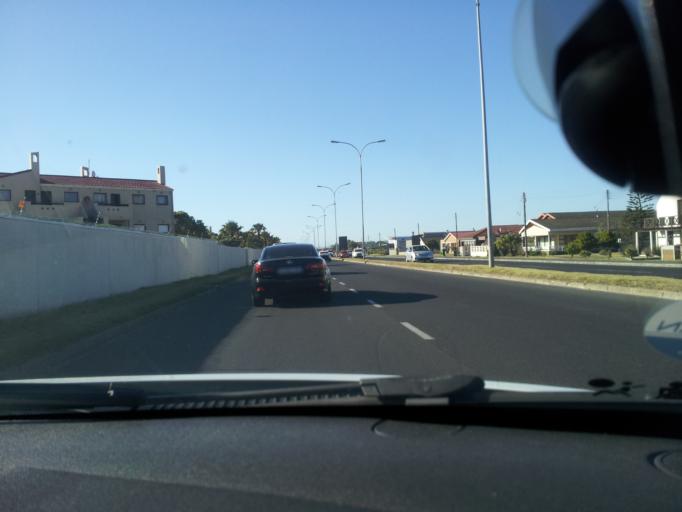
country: ZA
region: Western Cape
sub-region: Overberg District Municipality
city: Grabouw
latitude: -34.1337
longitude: 18.8455
